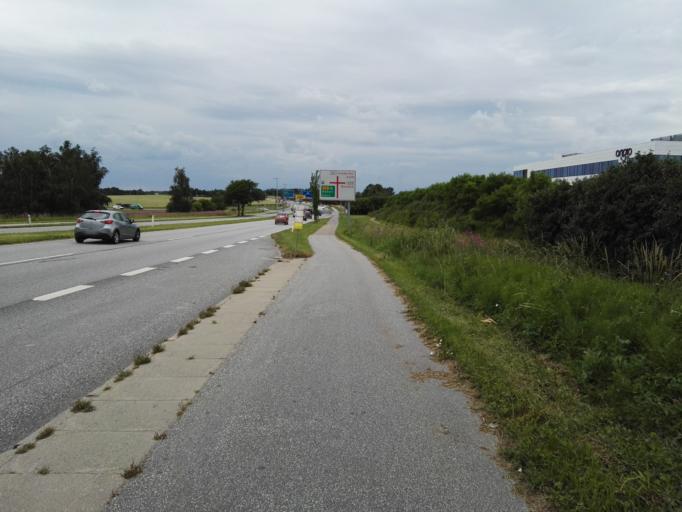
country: DK
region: Capital Region
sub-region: Egedal Kommune
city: Smorumnedre
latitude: 55.7543
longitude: 12.2915
